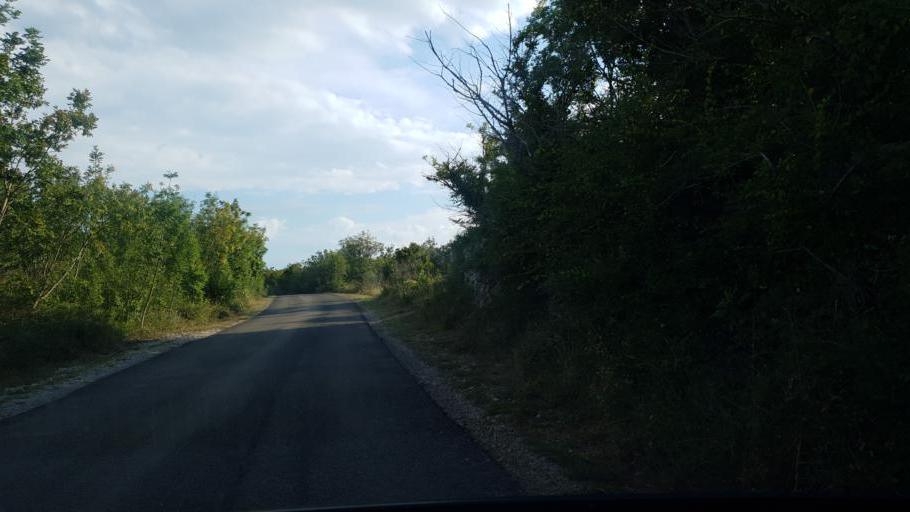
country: HR
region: Primorsko-Goranska
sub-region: Grad Crikvenica
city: Jadranovo
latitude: 45.1688
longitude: 14.6063
